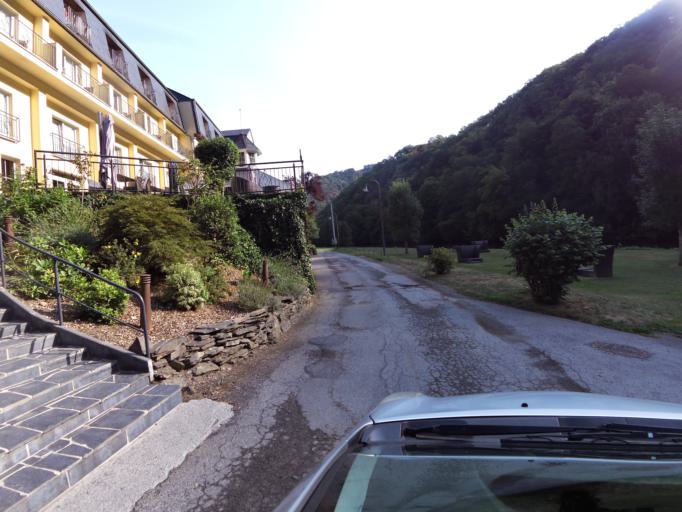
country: LU
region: Diekirch
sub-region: Canton de Diekirch
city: Bourscheid
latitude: 49.9085
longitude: 6.0808
